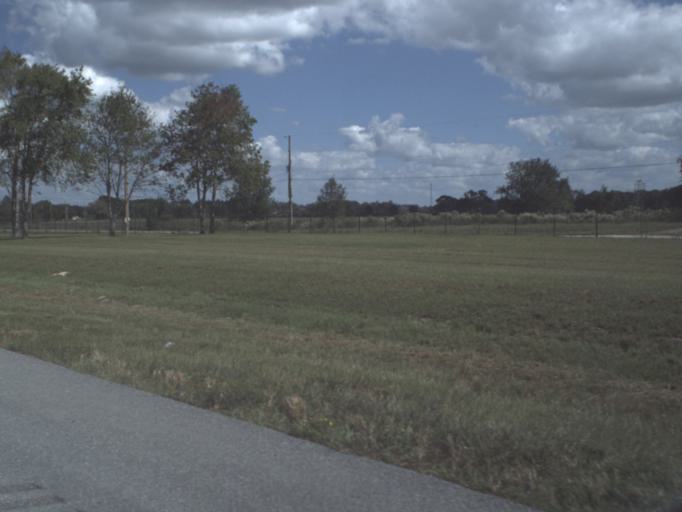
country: US
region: Florida
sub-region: Hernando County
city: Masaryktown
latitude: 28.4179
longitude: -82.4930
